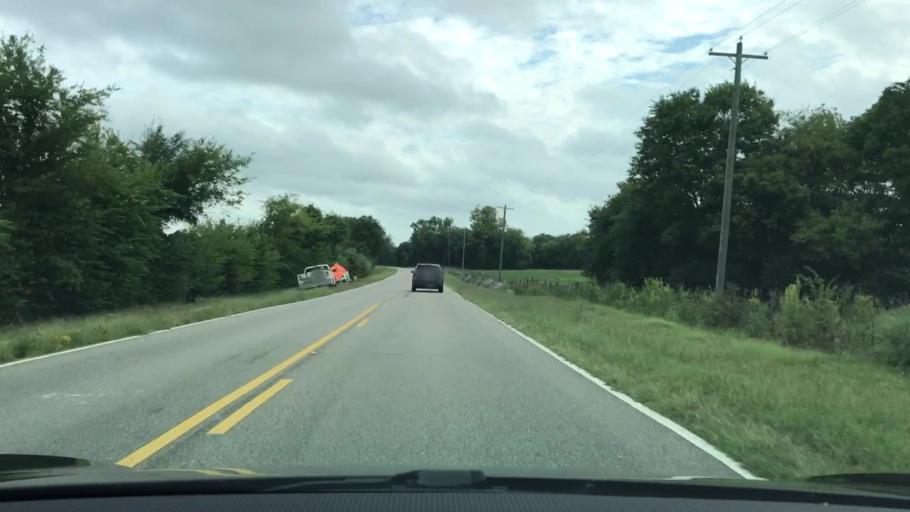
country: US
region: Alabama
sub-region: Montgomery County
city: Pike Road
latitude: 32.2914
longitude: -86.0754
